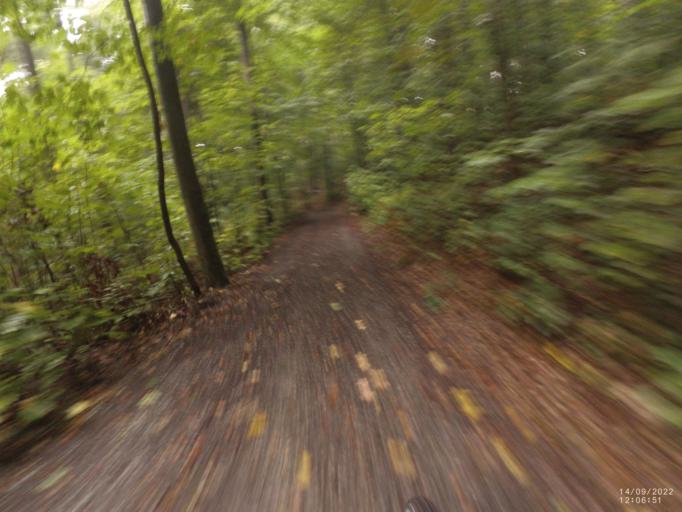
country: DE
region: Bavaria
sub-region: Regierungsbezirk Unterfranken
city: Johannesberg
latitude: 50.0157
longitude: 9.1365
